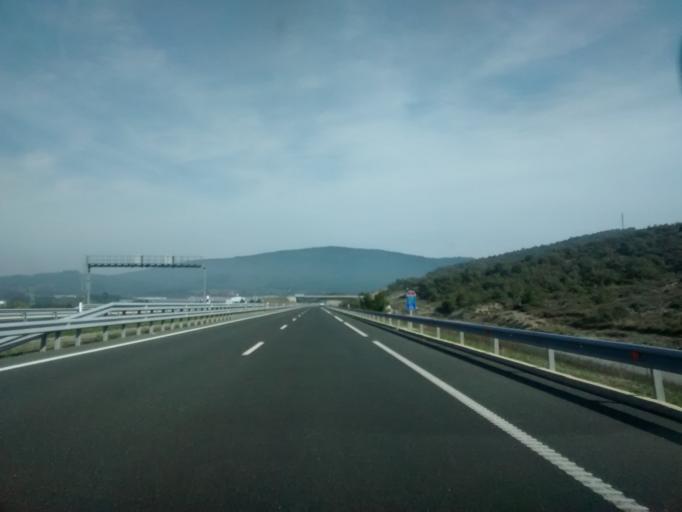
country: ES
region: Basque Country
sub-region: Provincia de Guipuzcoa
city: Leintz-Gatzaga
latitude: 42.9464
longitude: -2.6287
